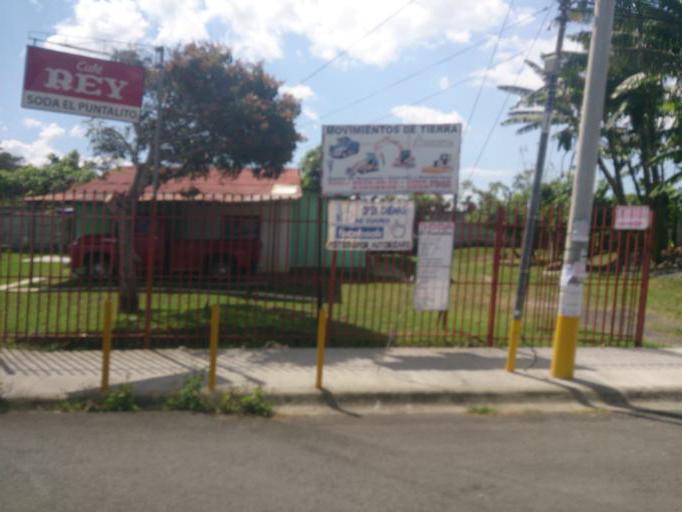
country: CR
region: San Jose
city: Granadilla
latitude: 9.9265
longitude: -84.0230
